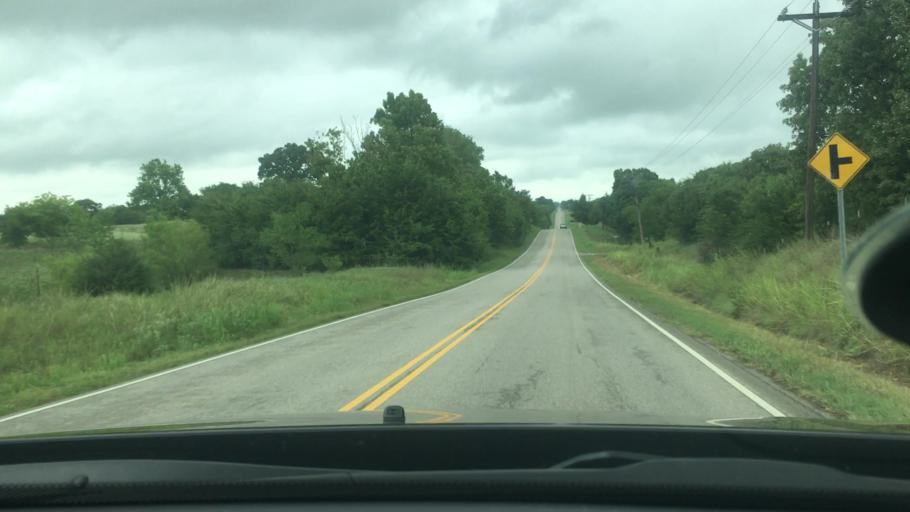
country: US
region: Oklahoma
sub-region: Bryan County
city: Calera
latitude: 33.9715
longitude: -96.5005
